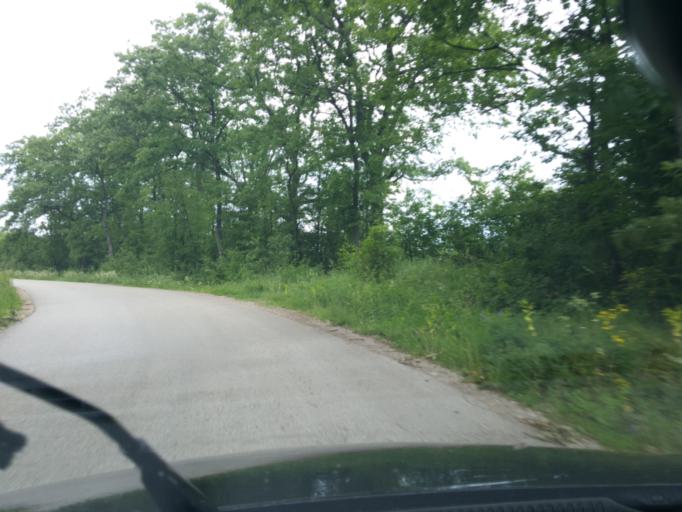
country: RS
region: Central Serbia
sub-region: Zajecarski Okrug
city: Boljevac
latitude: 43.8086
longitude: 21.8942
